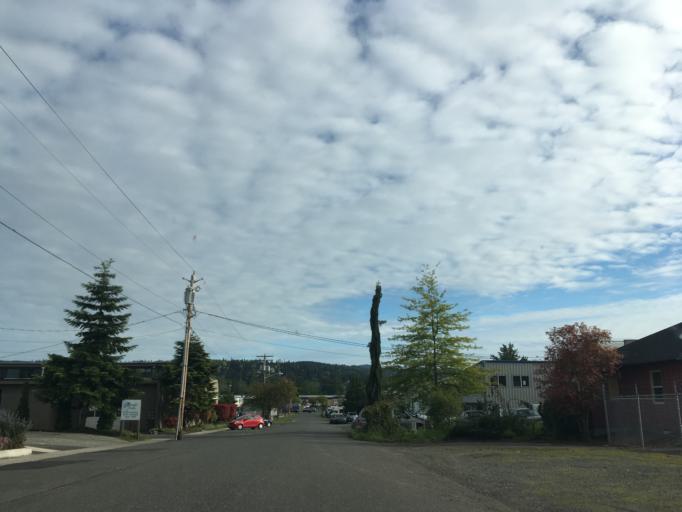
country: US
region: Washington
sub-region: Whatcom County
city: Bellingham
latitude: 48.7598
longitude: -122.4548
